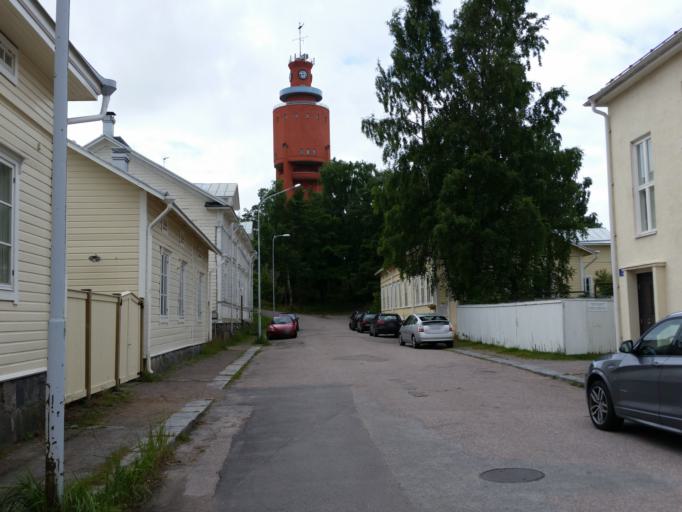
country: FI
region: Uusimaa
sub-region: Raaseporin
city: Hanko
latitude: 59.8256
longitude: 22.9730
